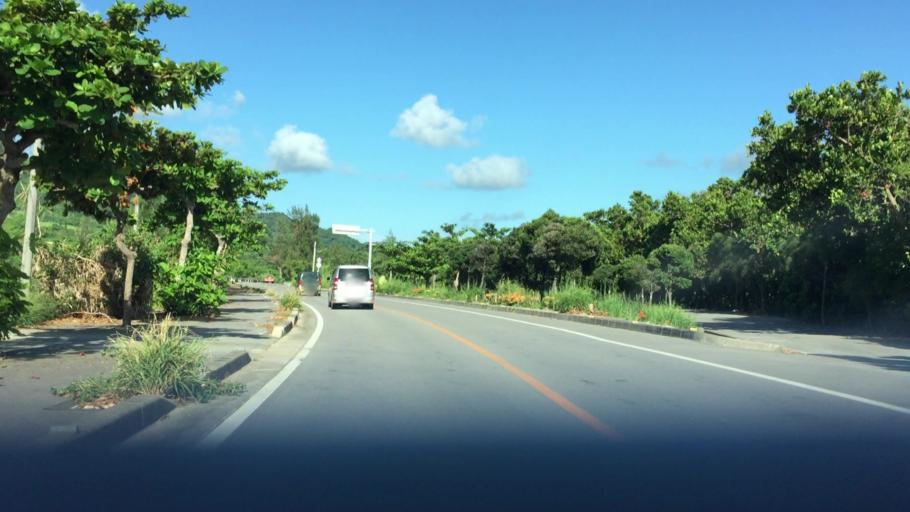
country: JP
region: Okinawa
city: Ishigaki
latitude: 24.4150
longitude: 124.1364
